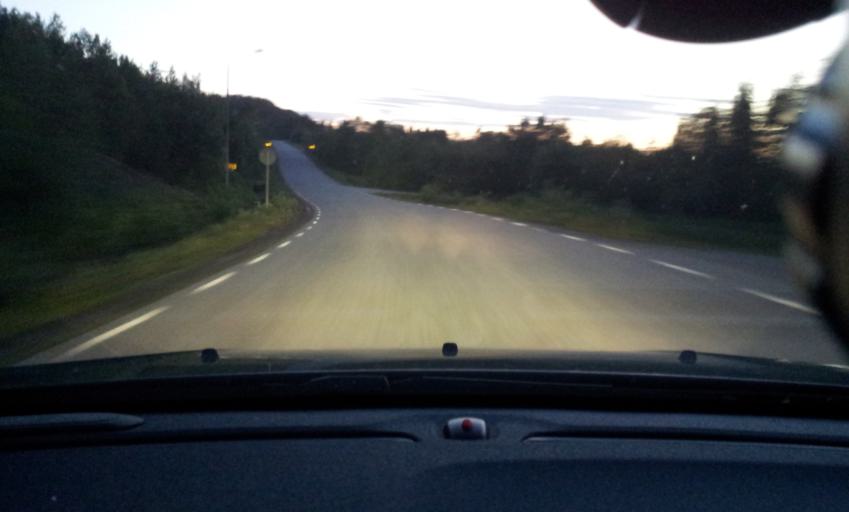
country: SE
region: Jaemtland
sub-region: Bergs Kommun
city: Hoverberg
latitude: 62.7645
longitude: 14.5570
